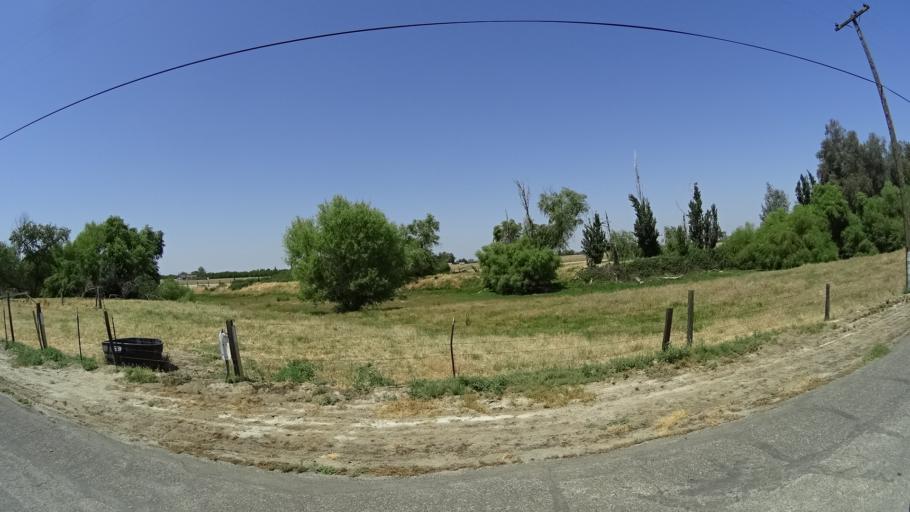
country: US
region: California
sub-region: Kings County
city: Armona
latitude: 36.2878
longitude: -119.6911
